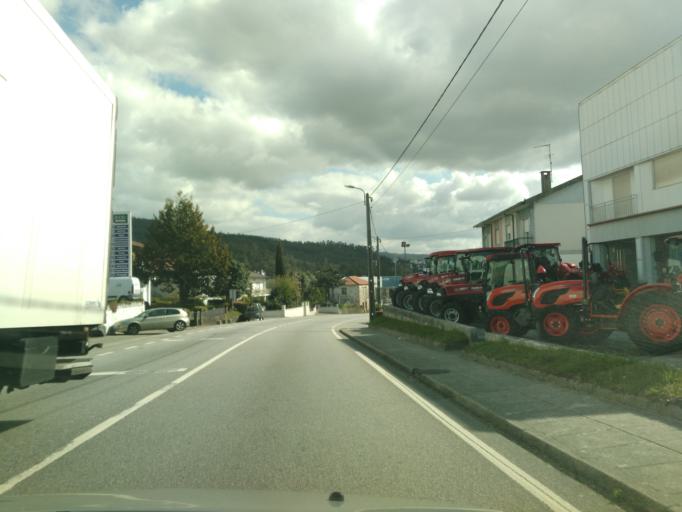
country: PT
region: Braga
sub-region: Braga
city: Braga
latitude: 41.5286
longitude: -8.4179
